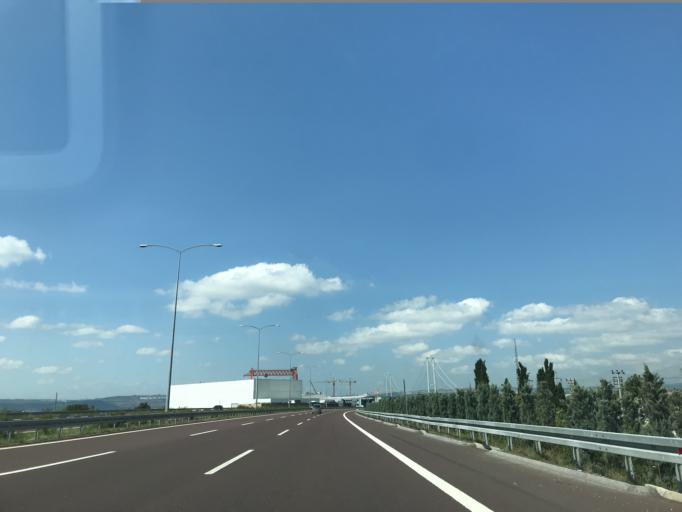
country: TR
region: Yalova
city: Altinova
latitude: 40.7224
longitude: 29.5031
